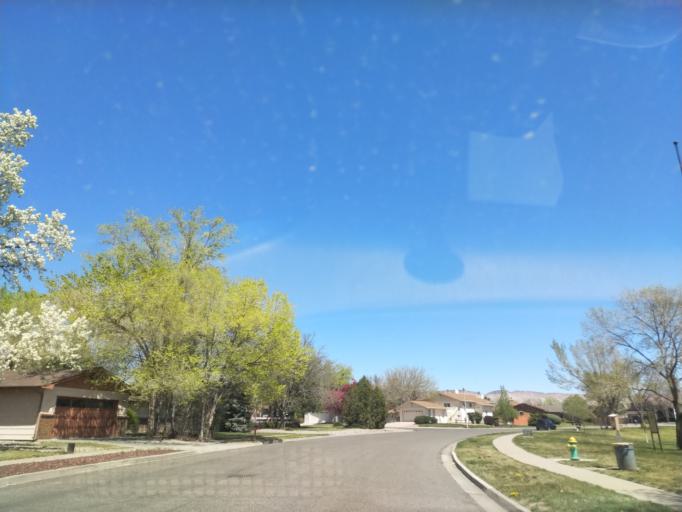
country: US
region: Colorado
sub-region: Mesa County
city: Grand Junction
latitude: 39.0937
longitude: -108.5387
